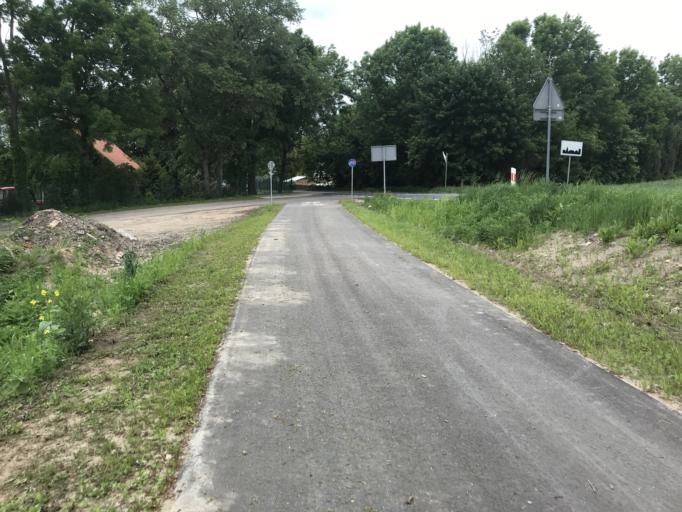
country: PL
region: West Pomeranian Voivodeship
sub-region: Powiat mysliborski
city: Debno
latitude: 52.6841
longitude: 14.6433
